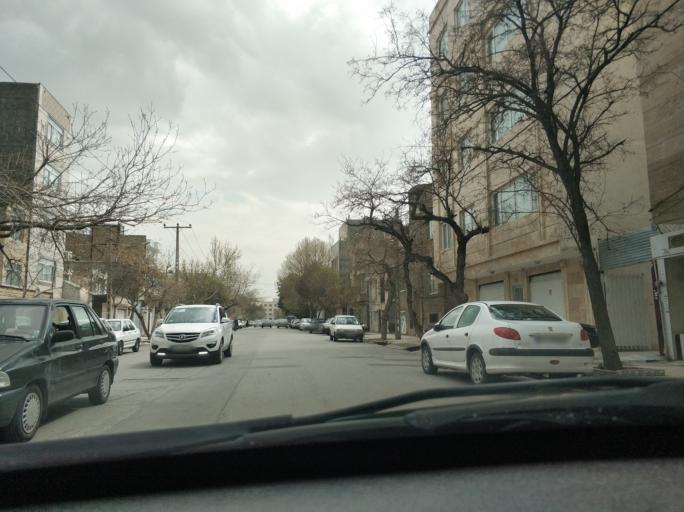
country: IR
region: Razavi Khorasan
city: Mashhad
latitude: 36.2749
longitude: 59.5724
